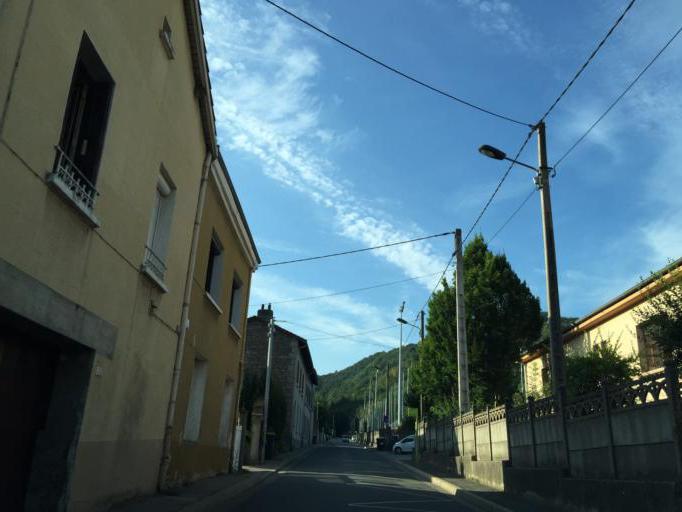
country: FR
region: Rhone-Alpes
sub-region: Departement de la Loire
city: Saint-Jean-Bonnefonds
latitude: 45.4274
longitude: 4.4356
